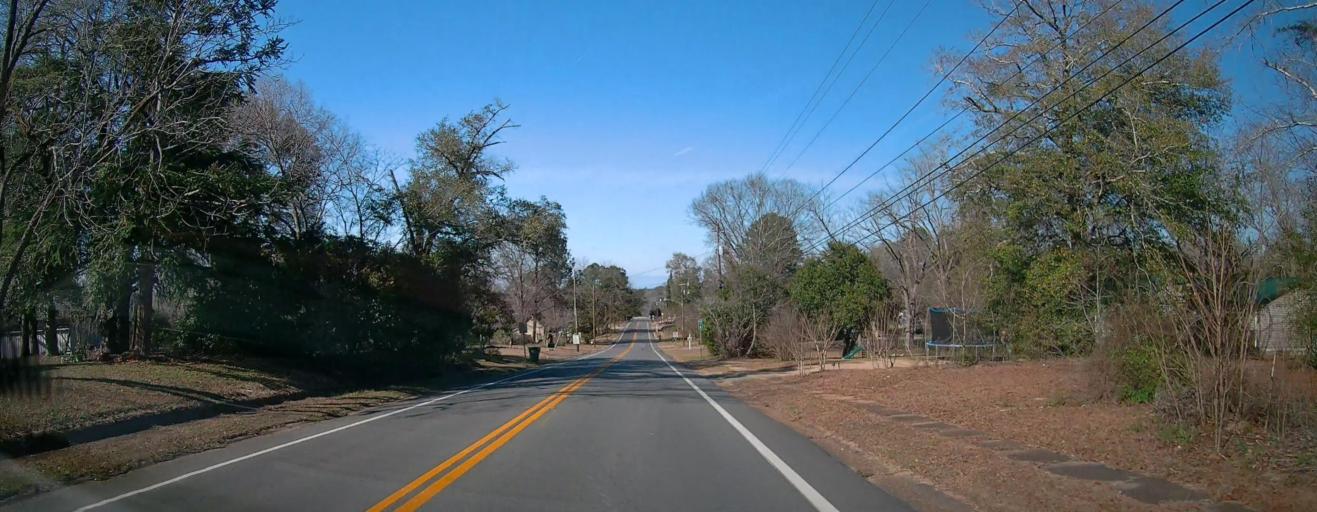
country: US
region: Georgia
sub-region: Macon County
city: Oglethorpe
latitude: 32.3713
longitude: -84.1883
